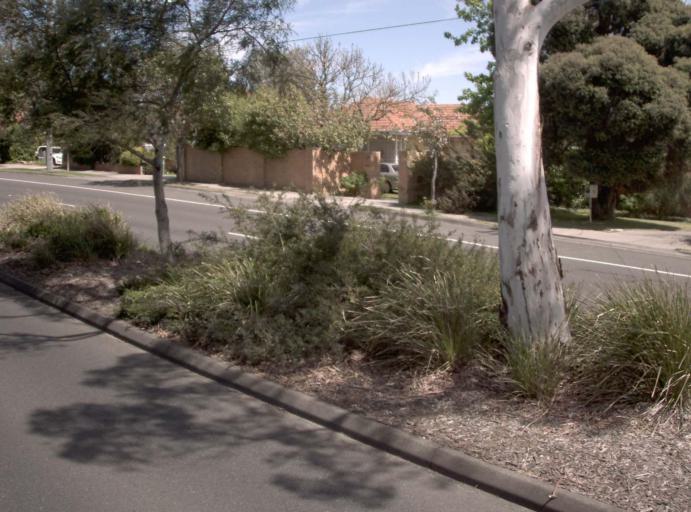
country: AU
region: Victoria
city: Burwood East
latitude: -37.8461
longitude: 145.1539
